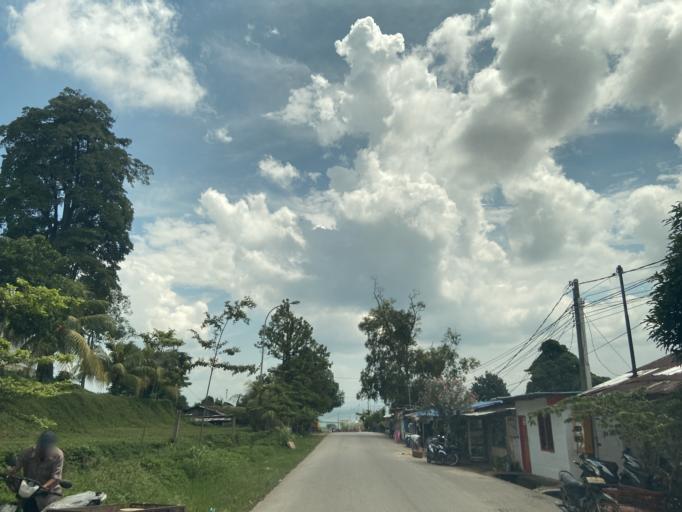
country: SG
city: Singapore
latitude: 1.1579
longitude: 104.0115
